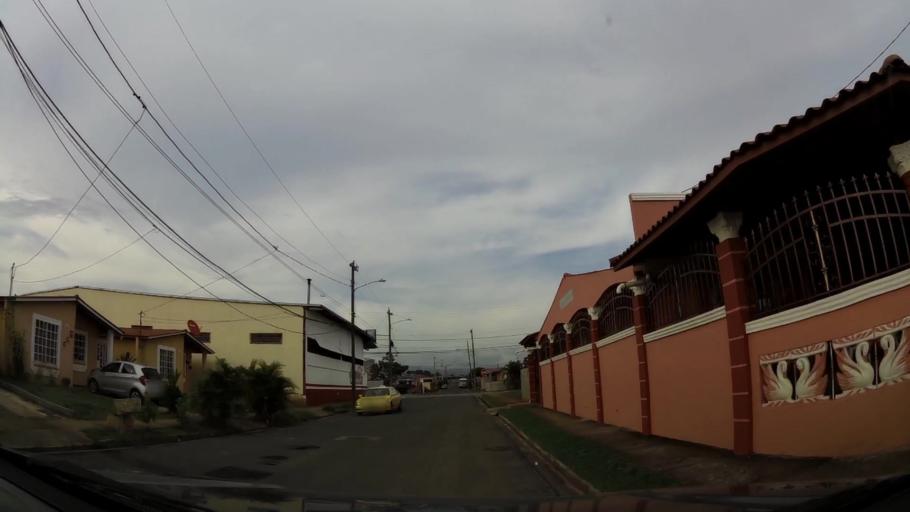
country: PA
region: Panama
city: Tocumen
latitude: 9.0734
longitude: -79.3631
